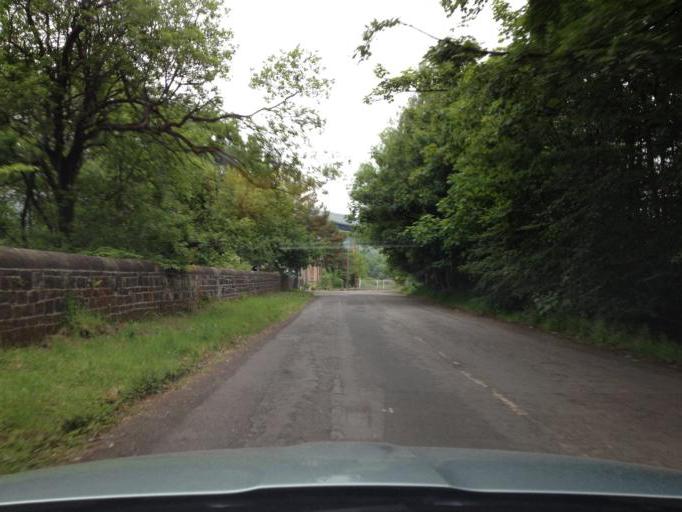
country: GB
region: Scotland
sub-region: West Dunbartonshire
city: Old Kilpatrick
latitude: 55.9163
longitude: -4.4623
